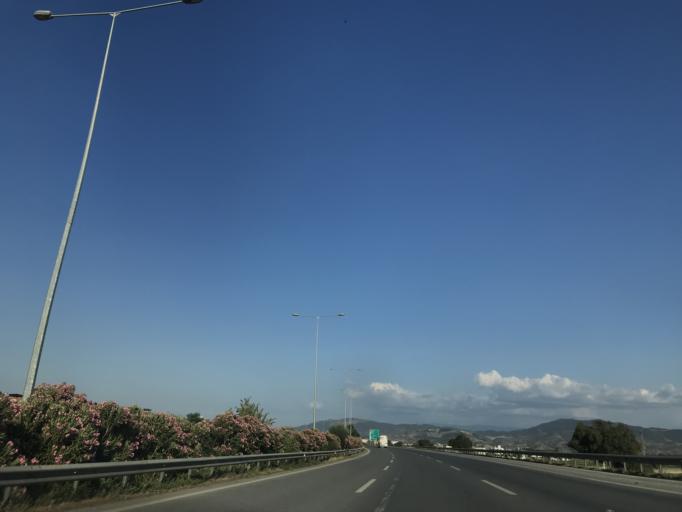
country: TR
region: Aydin
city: Aydin
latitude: 37.8223
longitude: 27.8191
